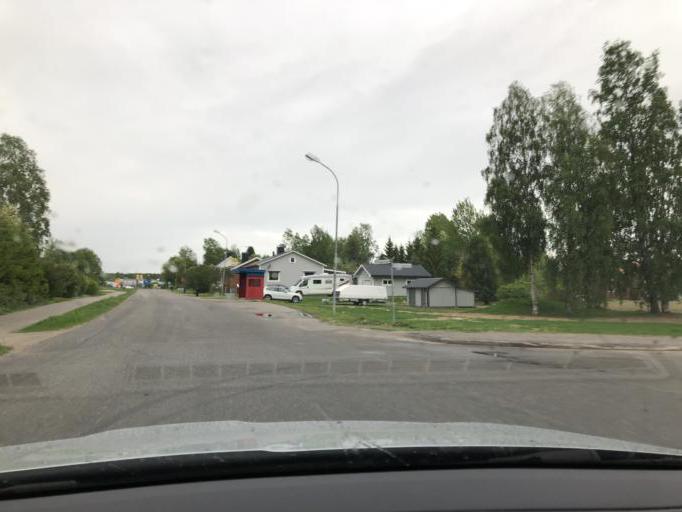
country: SE
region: Norrbotten
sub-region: Pitea Kommun
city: Bergsviken
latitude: 65.3405
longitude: 21.3991
